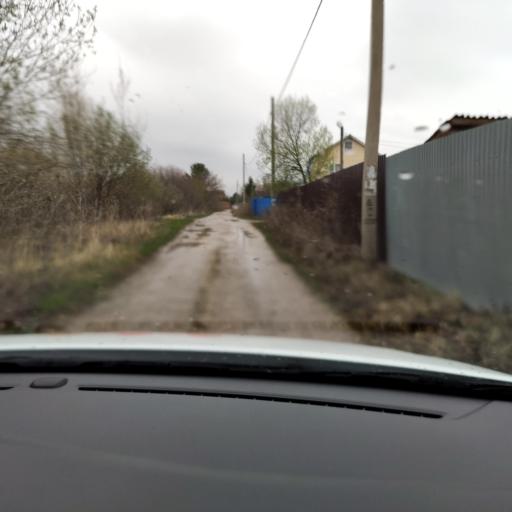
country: RU
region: Tatarstan
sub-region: Gorod Kazan'
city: Kazan
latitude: 55.6871
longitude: 49.0658
